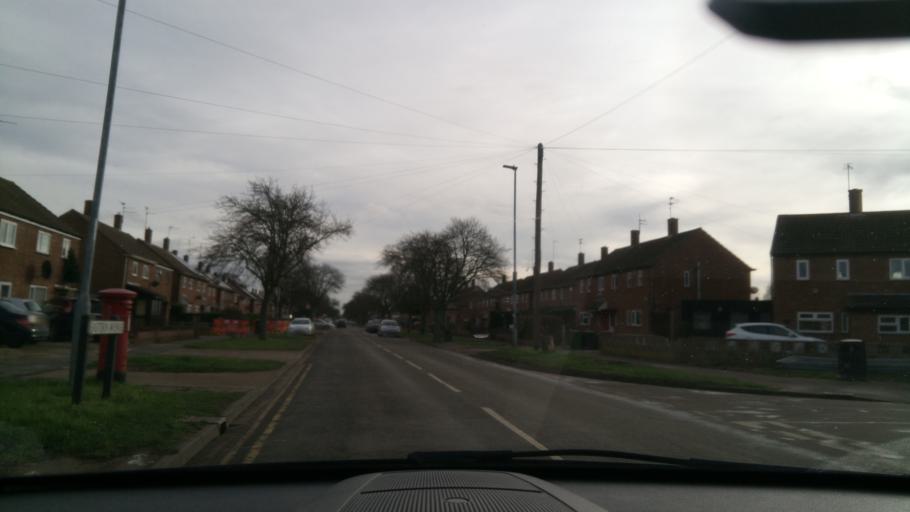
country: GB
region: England
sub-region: Peterborough
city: Peterborough
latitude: 52.6009
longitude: -0.2318
